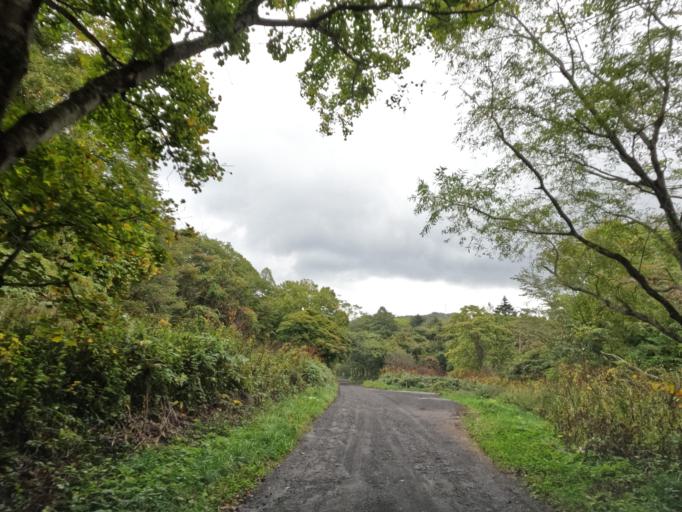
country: JP
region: Hokkaido
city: Date
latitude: 42.5011
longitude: 140.9155
